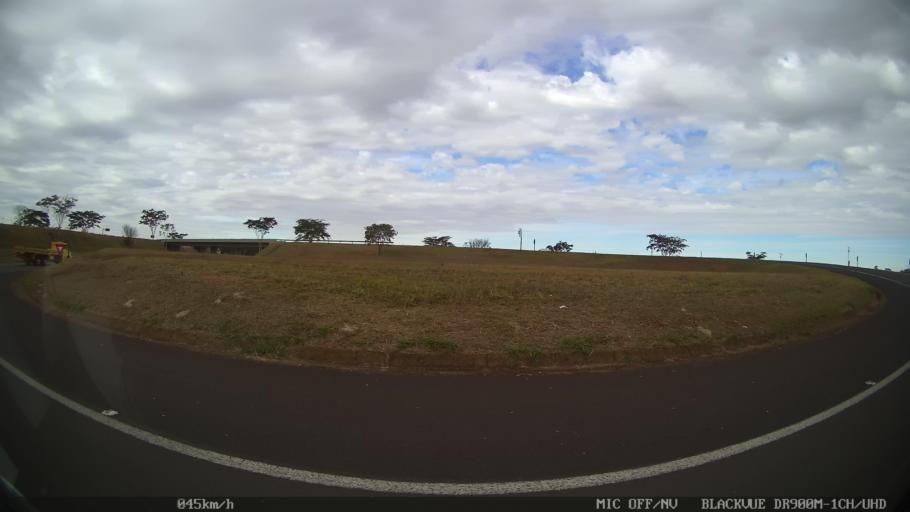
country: BR
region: Sao Paulo
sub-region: Bady Bassitt
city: Bady Bassitt
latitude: -20.8035
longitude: -49.5264
